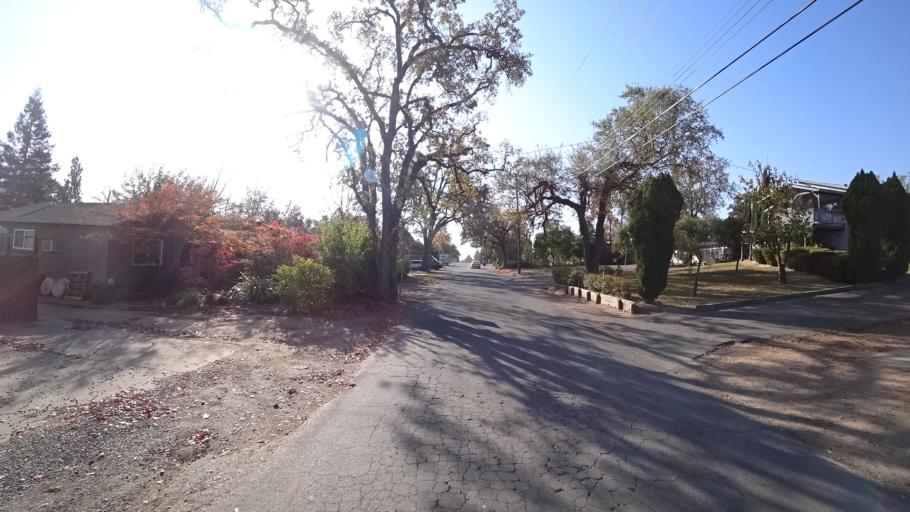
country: US
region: California
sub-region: Sacramento County
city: Citrus Heights
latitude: 38.6972
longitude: -121.2580
